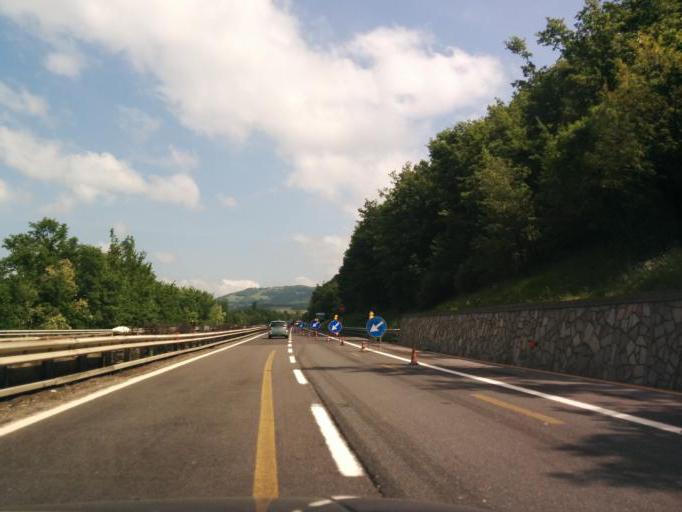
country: IT
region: Emilia-Romagna
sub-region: Provincia di Bologna
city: Castiglione dei Pepoli
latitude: 44.1643
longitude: 11.2088
